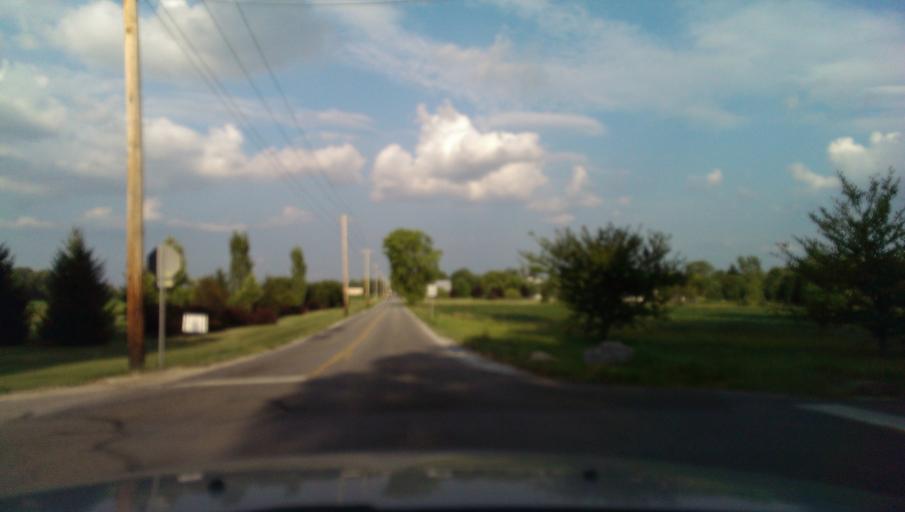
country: US
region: Indiana
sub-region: Hamilton County
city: Westfield
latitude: 40.0649
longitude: -86.1093
